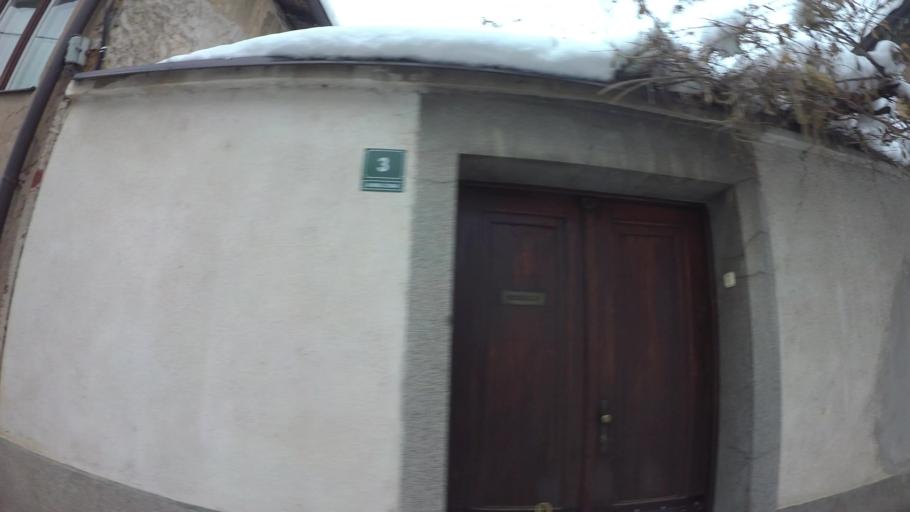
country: BA
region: Federation of Bosnia and Herzegovina
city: Kobilja Glava
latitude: 43.8654
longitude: 18.4346
